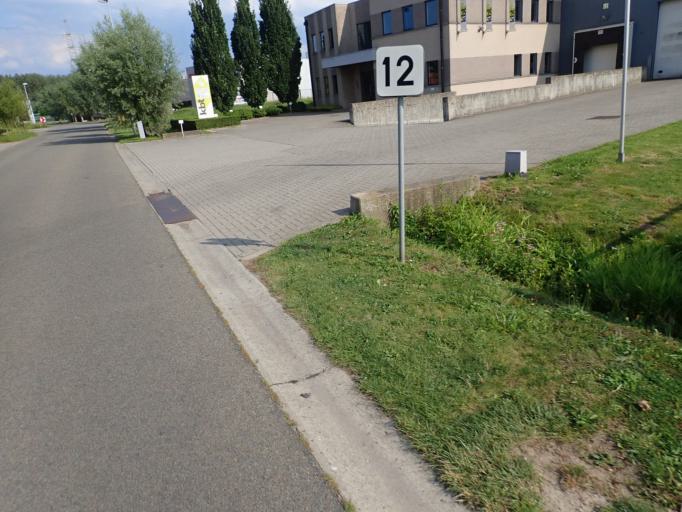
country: BE
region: Flanders
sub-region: Provincie Antwerpen
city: Sint-Amands
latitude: 51.0598
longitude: 4.2127
